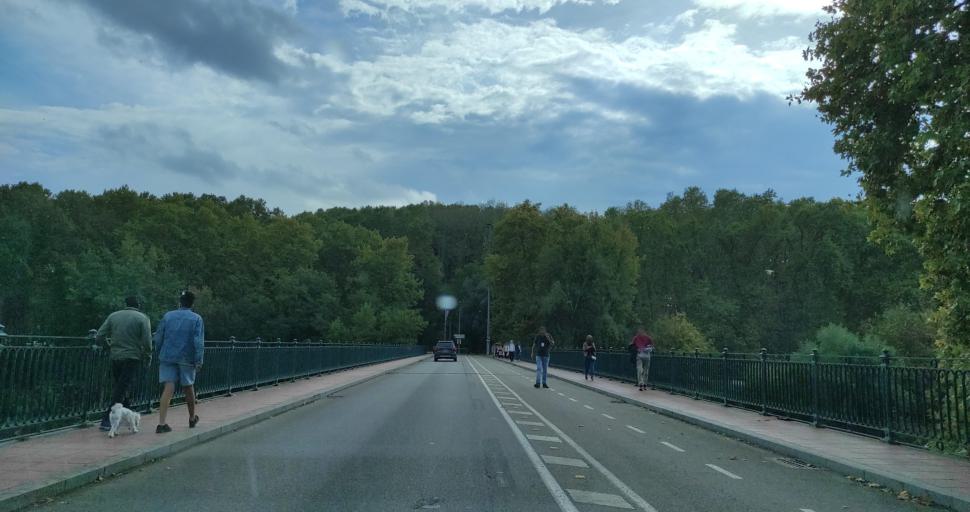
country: ES
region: Catalonia
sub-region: Provincia de Girona
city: Girona
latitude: 41.9909
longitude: 2.8189
